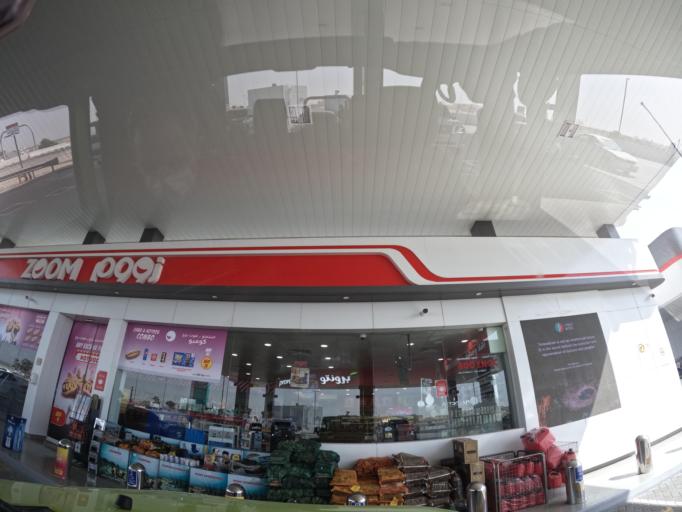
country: AE
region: Ash Shariqah
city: Sharjah
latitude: 25.1589
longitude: 55.3640
